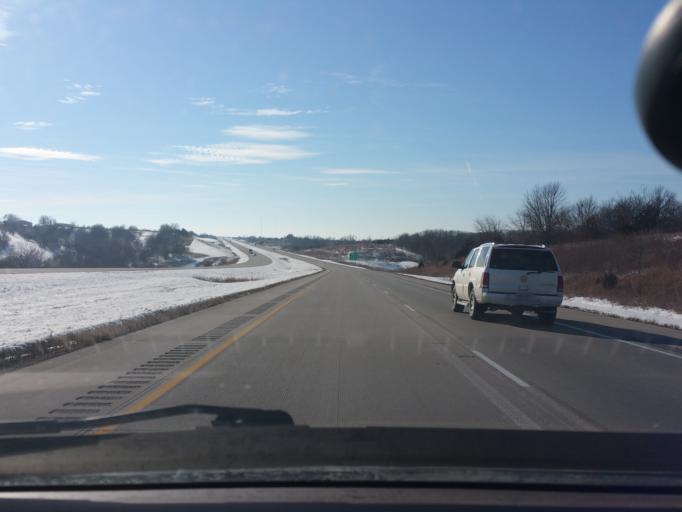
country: US
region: Iowa
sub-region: Clarke County
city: Osceola
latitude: 40.8927
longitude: -93.7997
